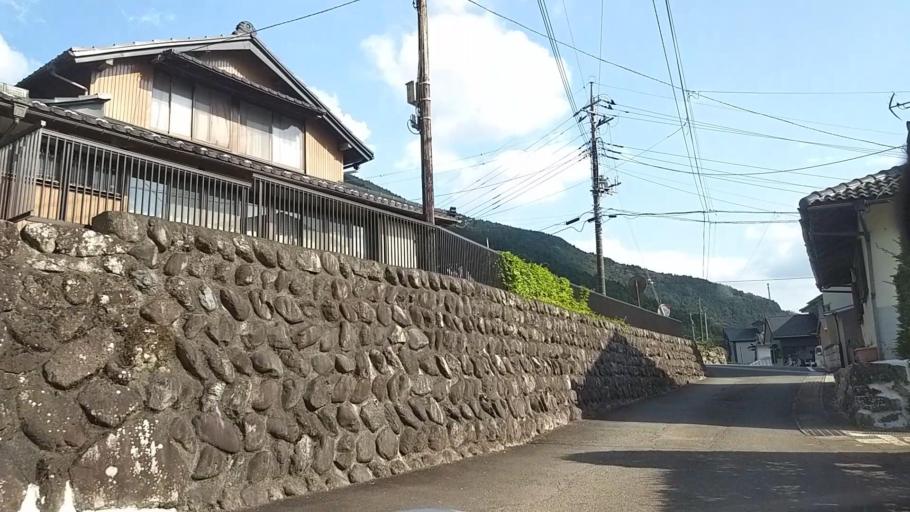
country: JP
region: Shizuoka
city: Fujinomiya
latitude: 35.2807
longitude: 138.4676
